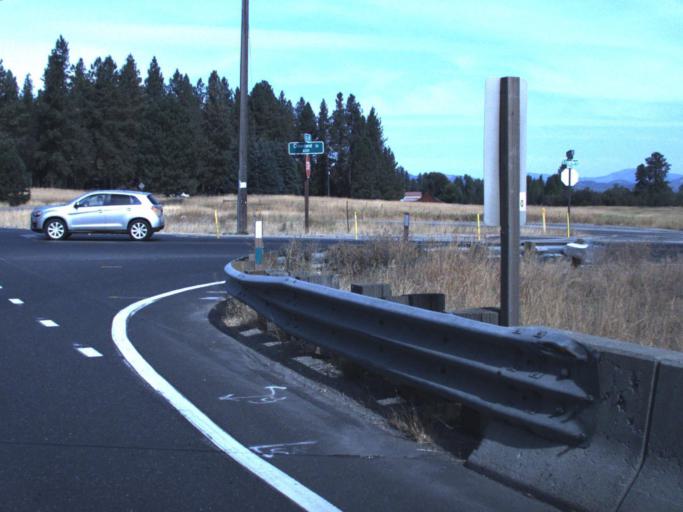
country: US
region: Washington
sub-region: Spokane County
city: Deer Park
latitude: 47.9540
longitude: -117.4882
